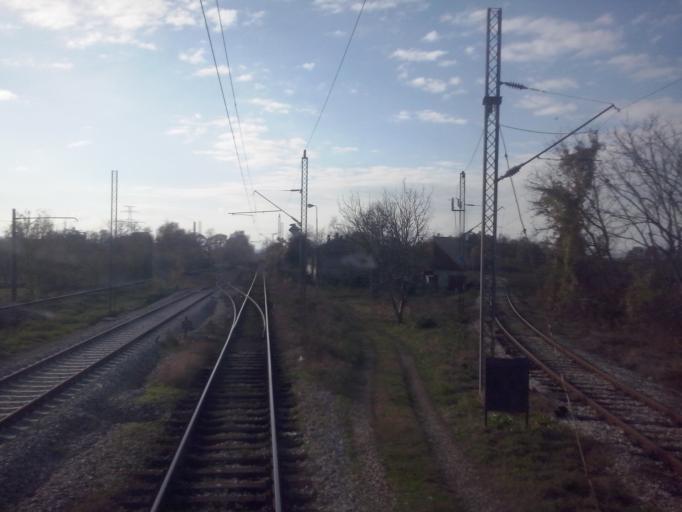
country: RS
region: Central Serbia
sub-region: Belgrade
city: Lazarevac
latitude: 44.4446
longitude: 20.2792
